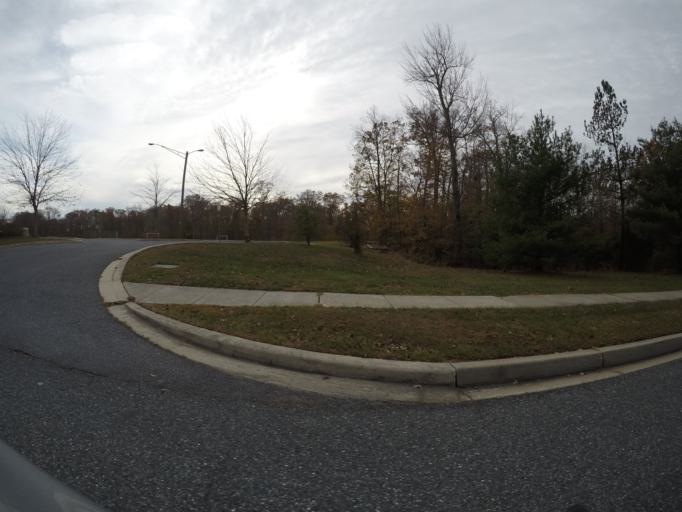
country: US
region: Maryland
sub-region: Harford County
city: Bel Air South
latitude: 39.4710
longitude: -76.3004
